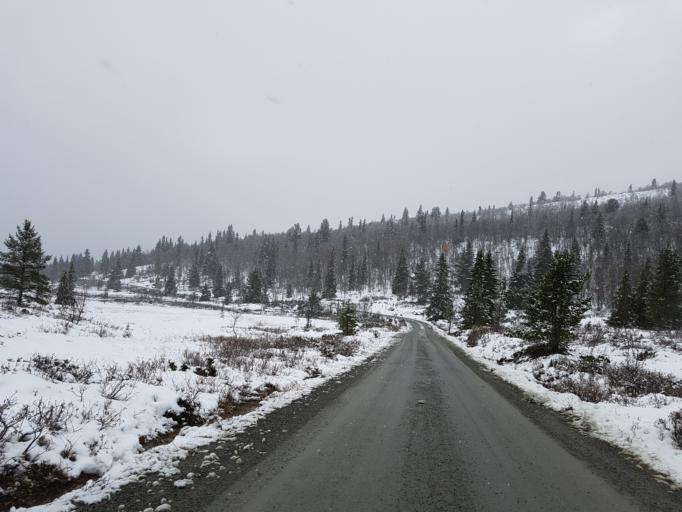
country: NO
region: Oppland
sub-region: Sel
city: Otta
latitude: 61.7959
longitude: 9.7146
